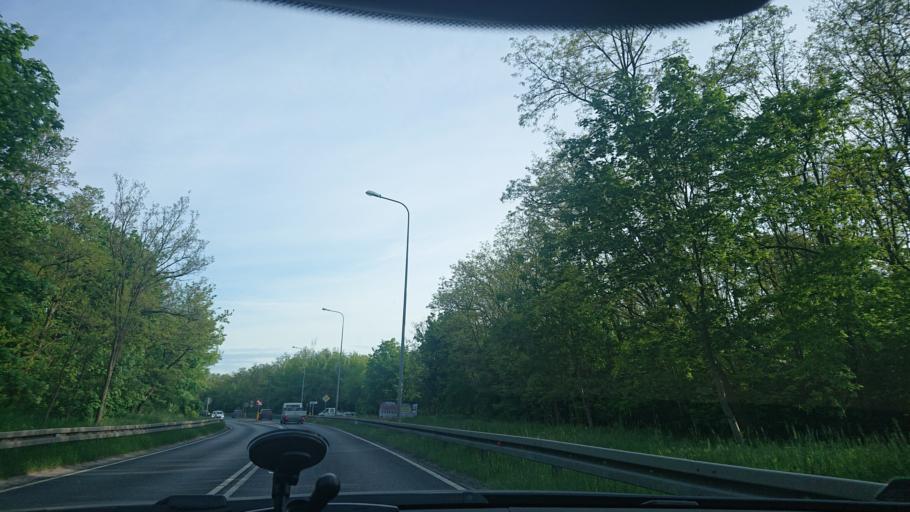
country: PL
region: Greater Poland Voivodeship
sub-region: Powiat gnieznienski
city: Gniezno
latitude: 52.5211
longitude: 17.5832
